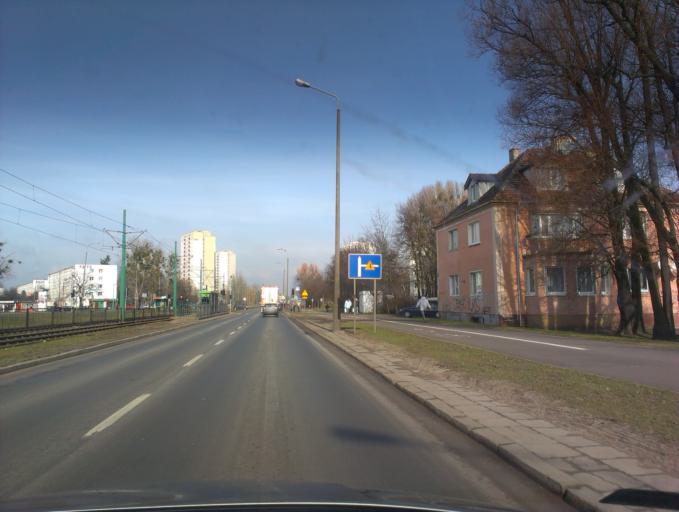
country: PL
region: Greater Poland Voivodeship
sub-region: Poznan
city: Poznan
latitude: 52.3890
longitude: 16.9469
